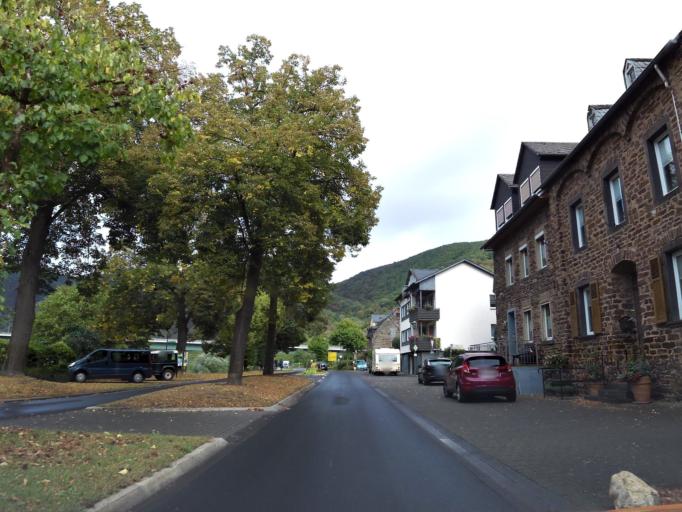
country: DE
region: Rheinland-Pfalz
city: Bruttig-Fankel
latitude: 50.1355
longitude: 7.2349
